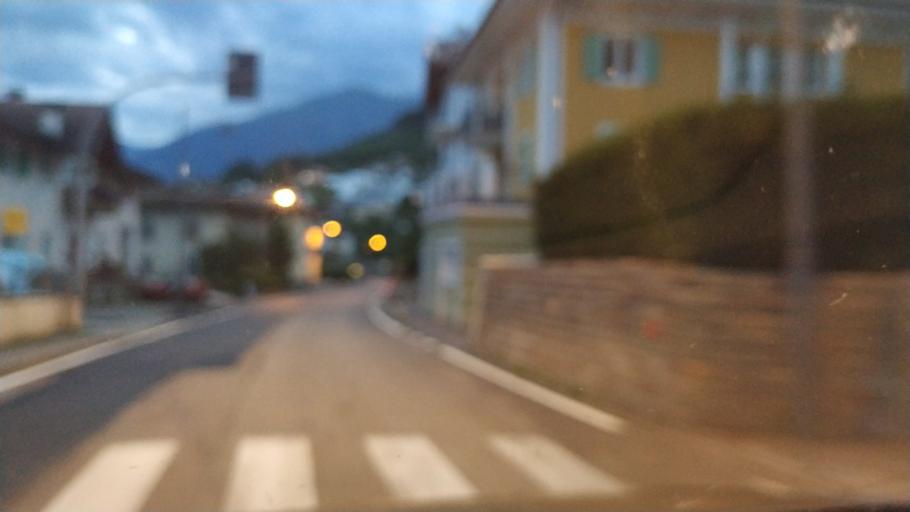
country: IT
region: Trentino-Alto Adige
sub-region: Provincia di Trento
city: Revo
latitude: 46.3913
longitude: 11.0570
